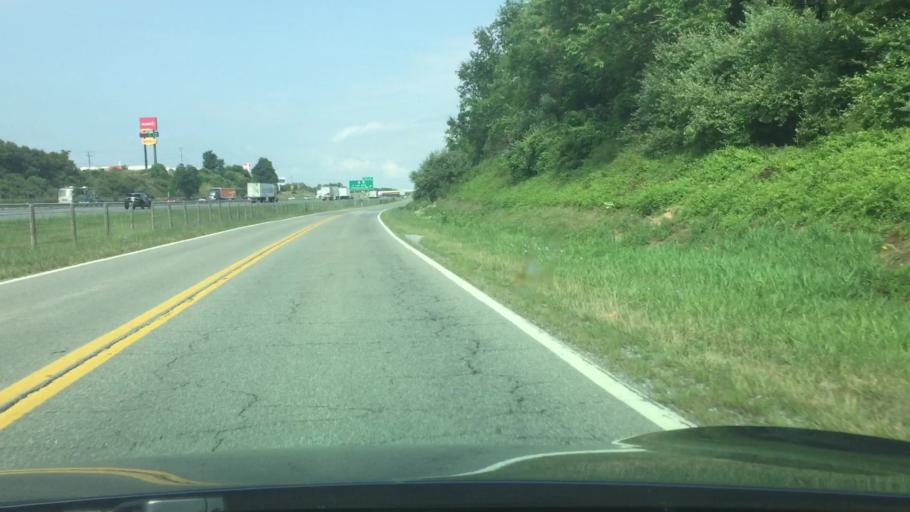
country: US
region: Virginia
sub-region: Wythe County
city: Wytheville
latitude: 36.9357
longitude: -80.9859
